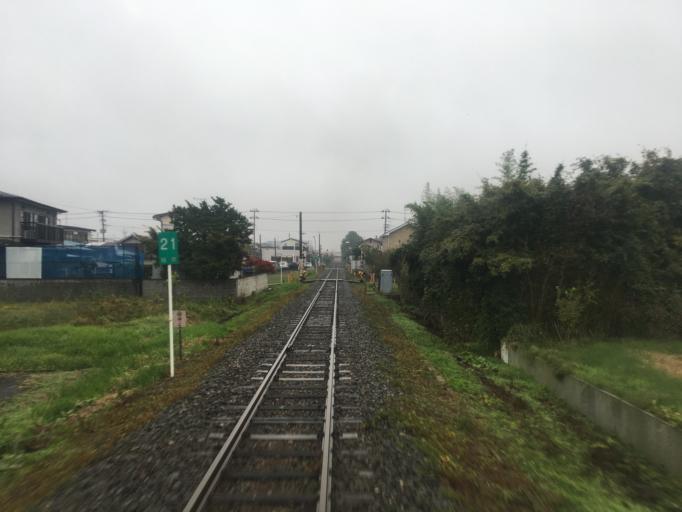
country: JP
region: Miyagi
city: Furukawa
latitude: 38.5716
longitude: 140.9533
